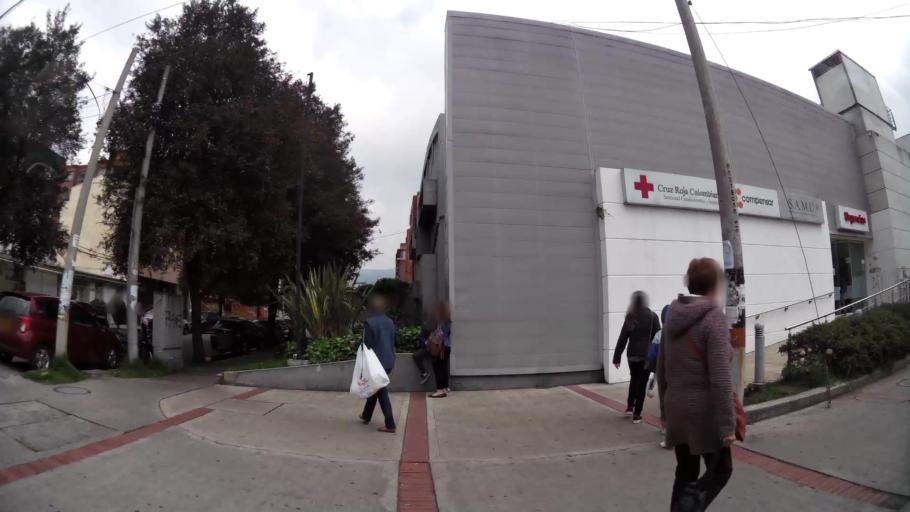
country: CO
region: Bogota D.C.
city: Barrio San Luis
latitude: 4.7278
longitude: -74.0496
